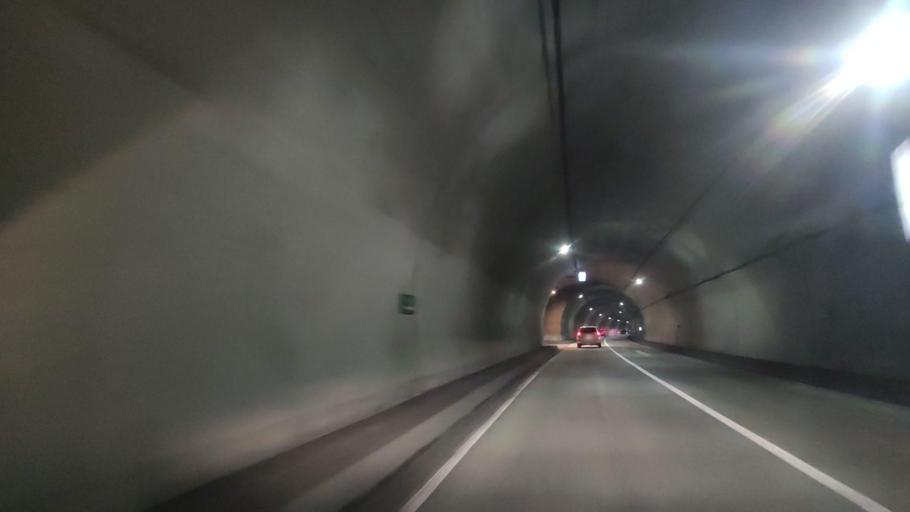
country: JP
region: Hokkaido
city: Ishikari
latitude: 43.5252
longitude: 141.3937
